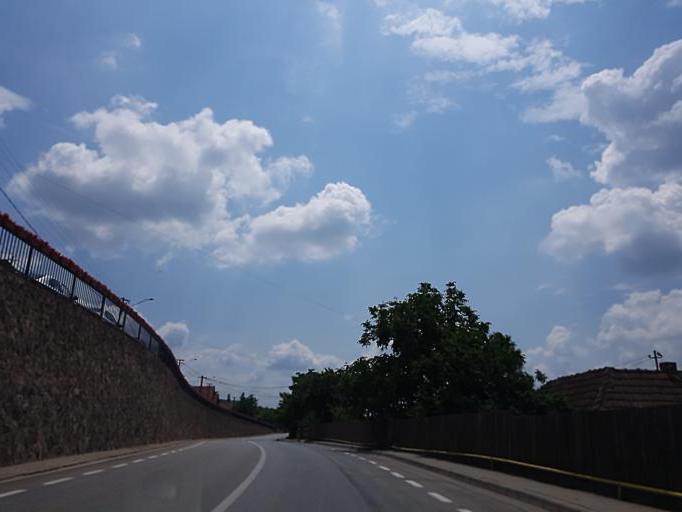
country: RO
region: Alba
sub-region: Municipiul Blaj
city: Veza
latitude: 46.1720
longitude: 23.9414
